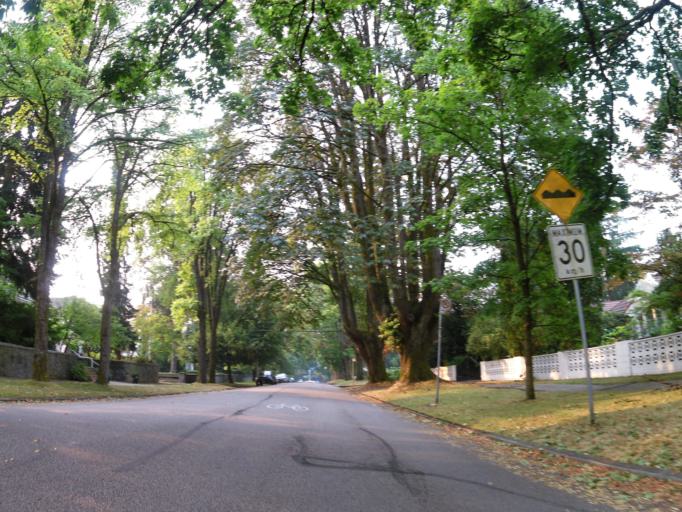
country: CA
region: British Columbia
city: Vancouver
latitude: 49.2494
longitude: -123.1462
